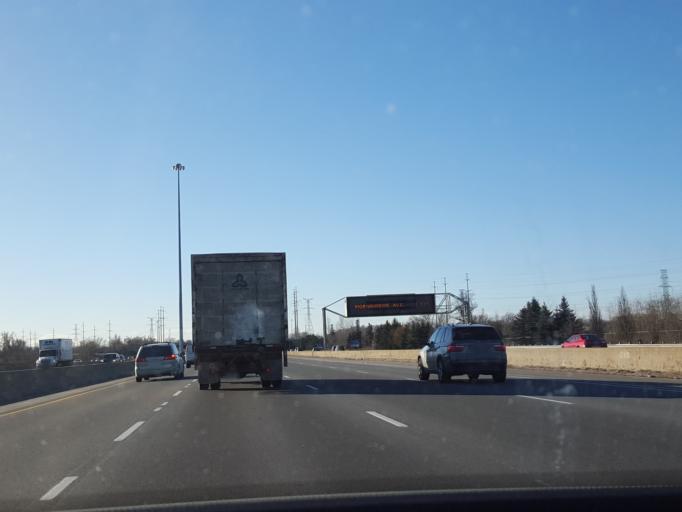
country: CA
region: Ontario
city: Scarborough
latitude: 43.7989
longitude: -79.1801
